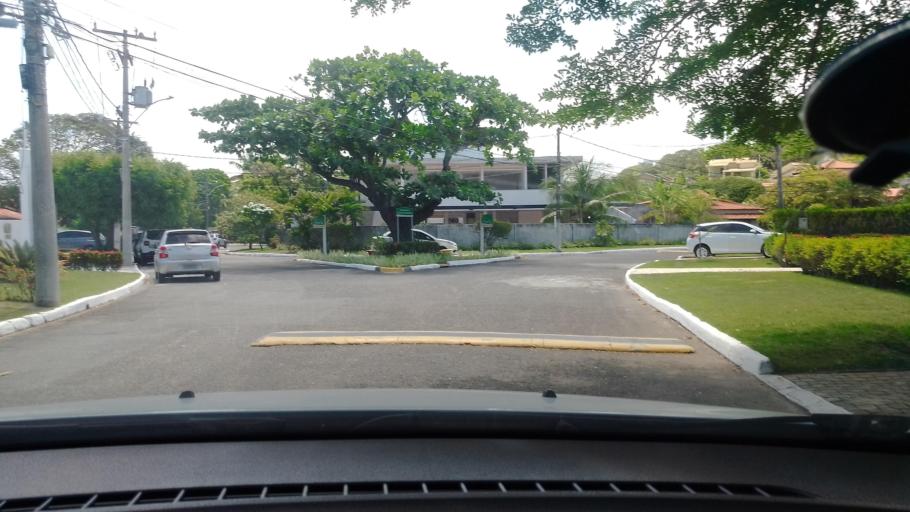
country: BR
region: Bahia
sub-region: Lauro De Freitas
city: Lauro de Freitas
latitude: -12.9542
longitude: -38.3942
